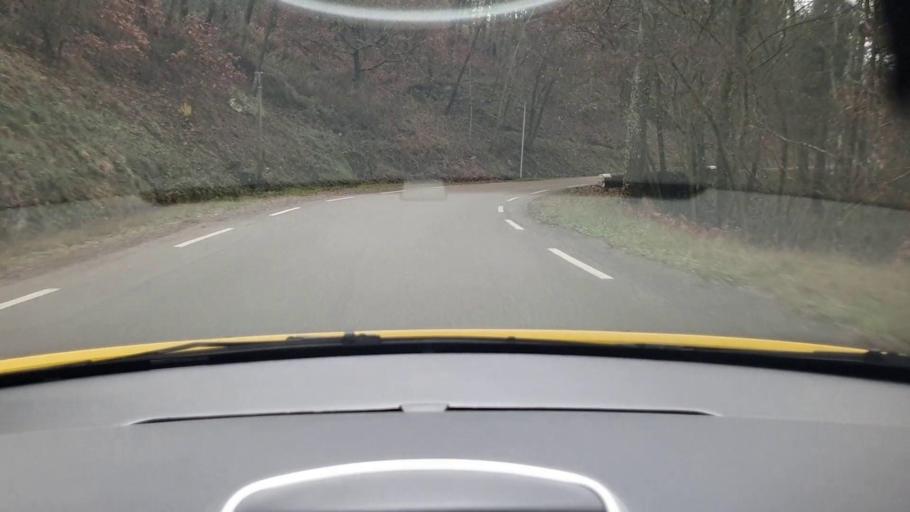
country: FR
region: Languedoc-Roussillon
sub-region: Departement du Gard
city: Besseges
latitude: 44.3152
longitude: 4.1374
